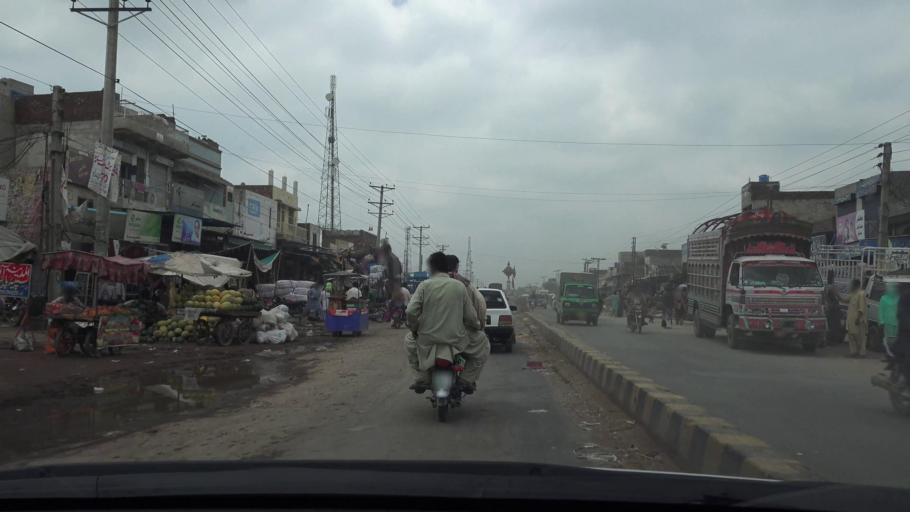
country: PK
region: Punjab
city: Faisalabad
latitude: 31.3880
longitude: 73.1986
